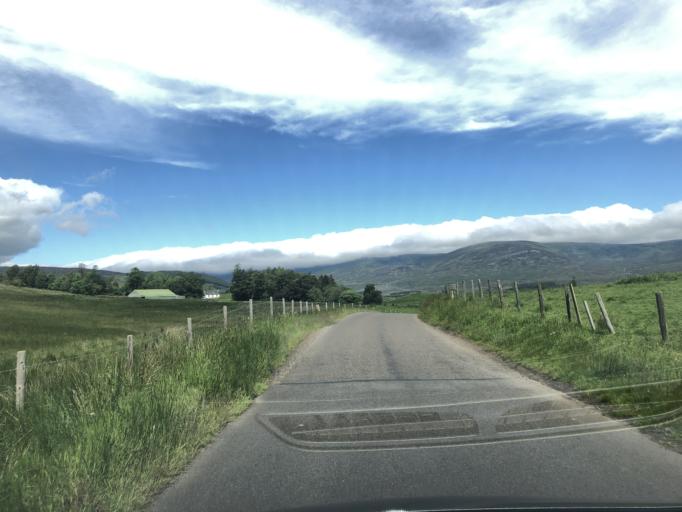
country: GB
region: Scotland
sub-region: Angus
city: Kirriemuir
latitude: 56.7906
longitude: -3.0444
